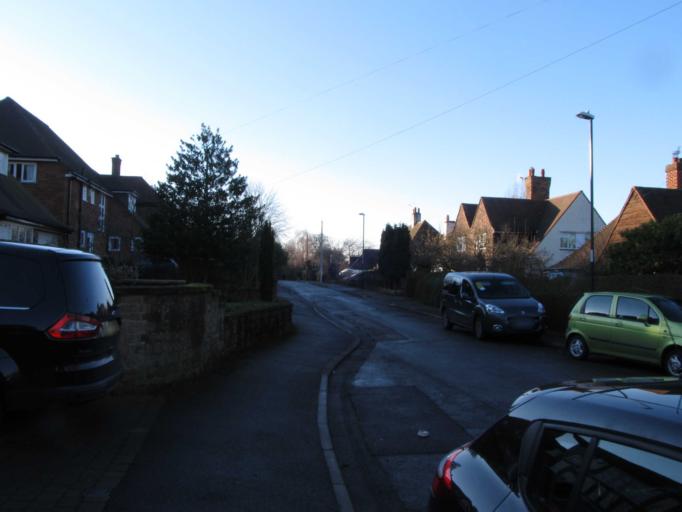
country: GB
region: England
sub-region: Nottingham
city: Nottingham
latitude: 52.9476
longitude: -1.1929
